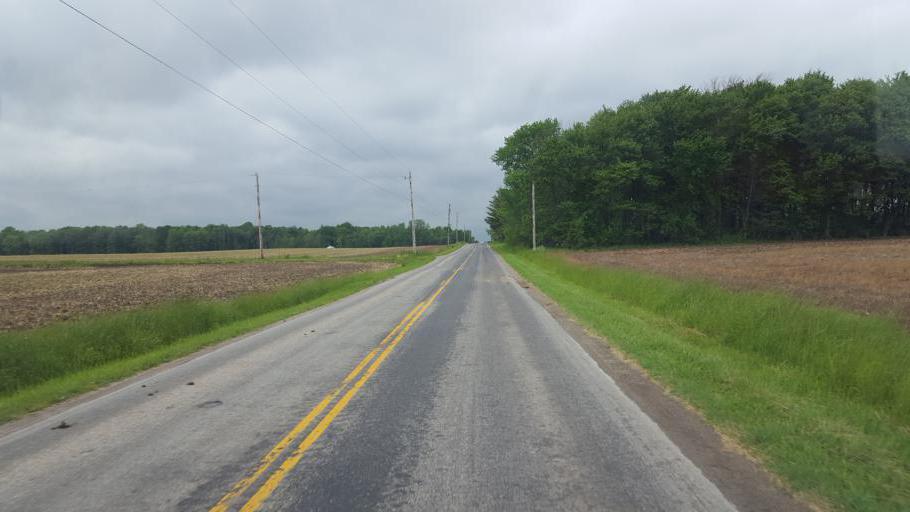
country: US
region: Ohio
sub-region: Wayne County
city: West Salem
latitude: 40.9515
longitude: -82.1621
